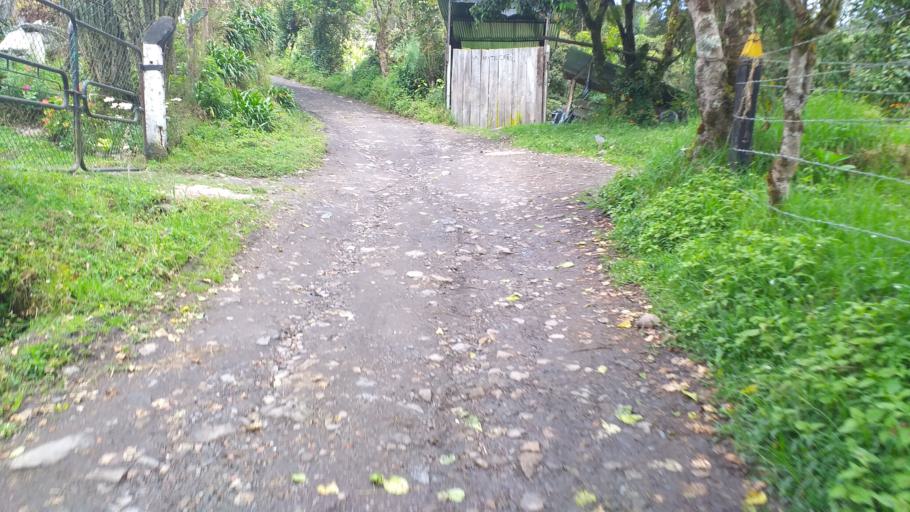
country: CO
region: Cundinamarca
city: Tenza
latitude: 5.1228
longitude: -73.4571
